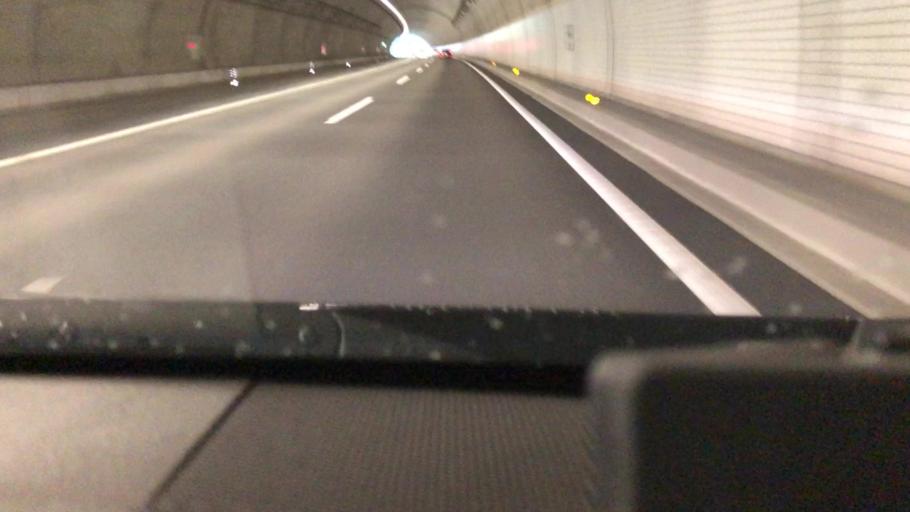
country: JP
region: Shizuoka
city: Kakegawa
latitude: 34.8417
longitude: 138.0232
